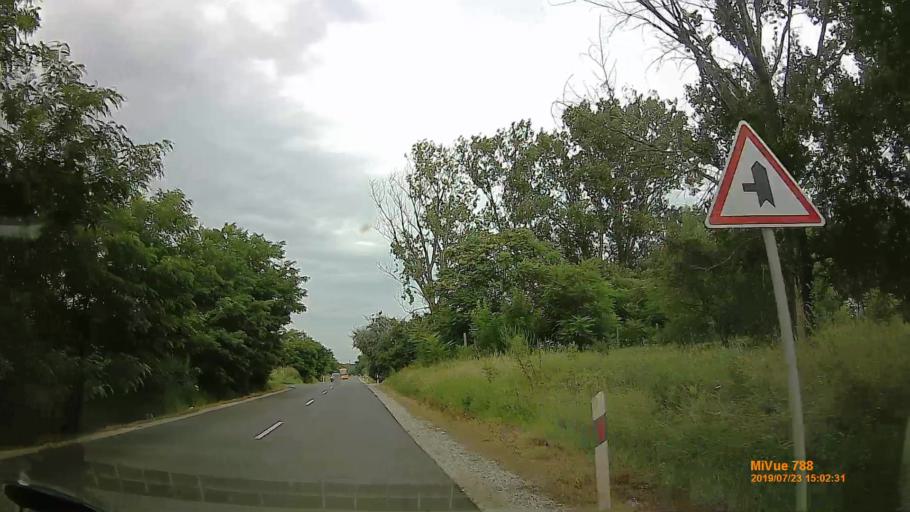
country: HU
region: Szabolcs-Szatmar-Bereg
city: Nyiregyhaza
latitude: 47.9318
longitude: 21.6997
